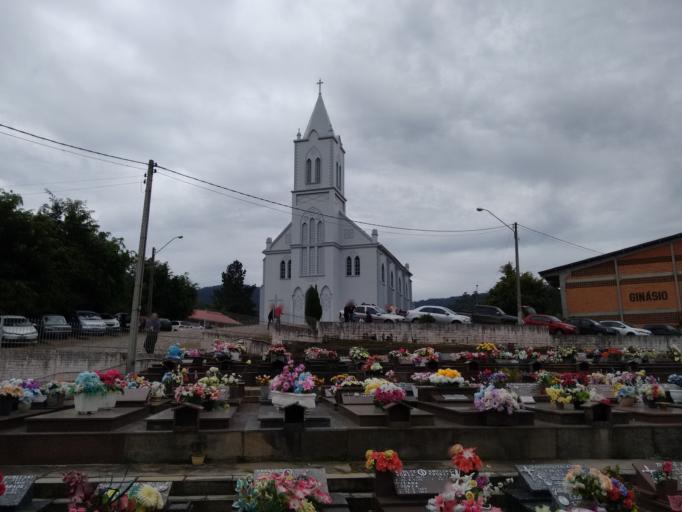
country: BR
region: Santa Catarina
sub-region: Rio Do Sul
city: Rio do Sul
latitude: -27.1457
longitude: -49.6200
